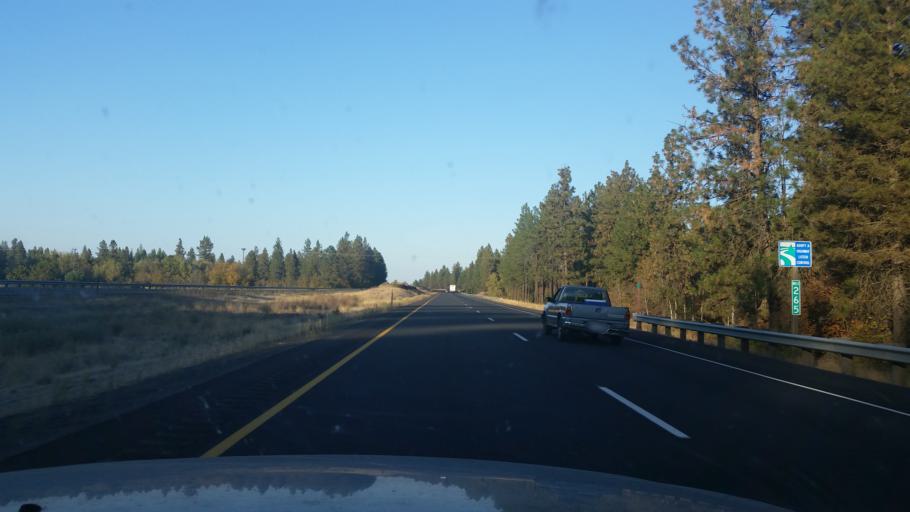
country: US
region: Washington
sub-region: Spokane County
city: Medical Lake
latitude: 47.5108
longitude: -117.6808
